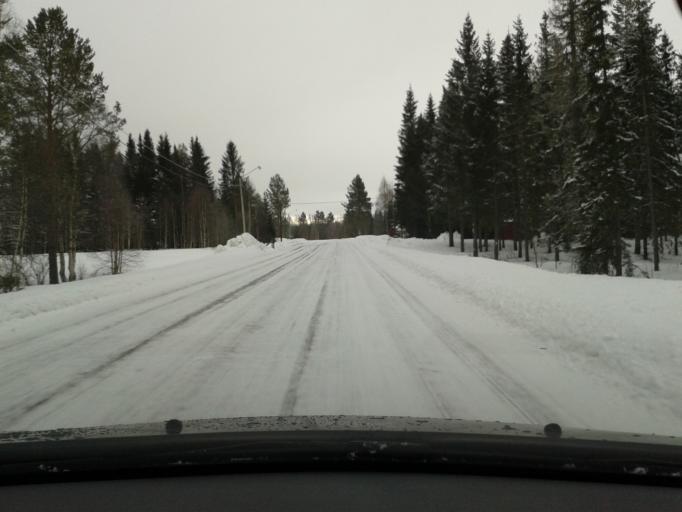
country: SE
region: Vaesterbotten
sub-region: Vilhelmina Kommun
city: Sjoberg
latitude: 64.8376
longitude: 15.9233
